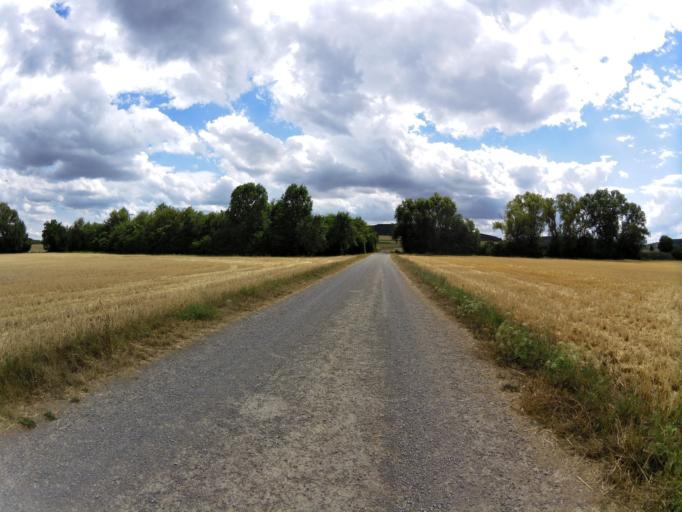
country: DE
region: Bavaria
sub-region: Regierungsbezirk Unterfranken
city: Zellingen
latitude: 49.8860
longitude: 9.8199
